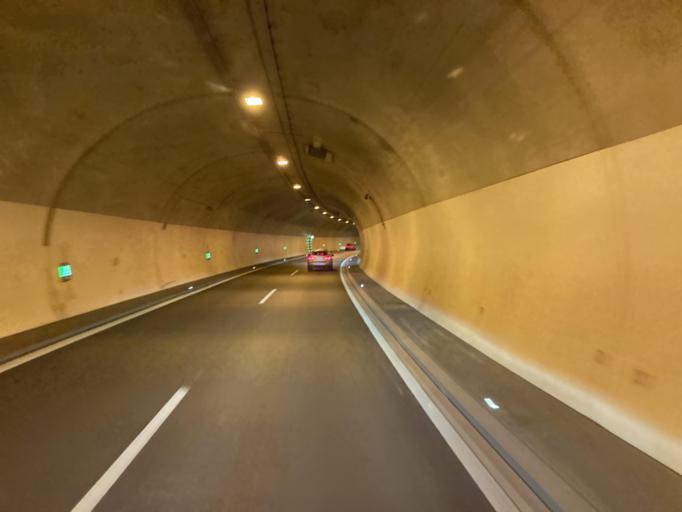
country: DE
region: Baden-Wuerttemberg
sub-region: Regierungsbezirk Stuttgart
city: Leutenbach
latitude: 48.8848
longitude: 9.3978
